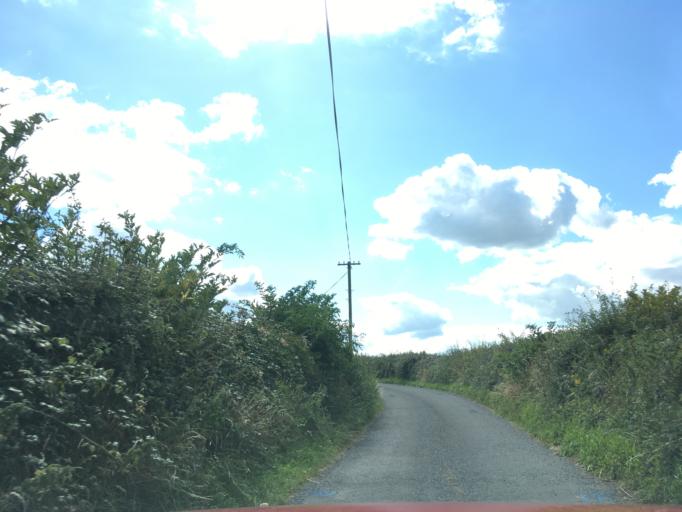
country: IE
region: Munster
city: Cashel
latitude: 52.4826
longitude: -7.9716
